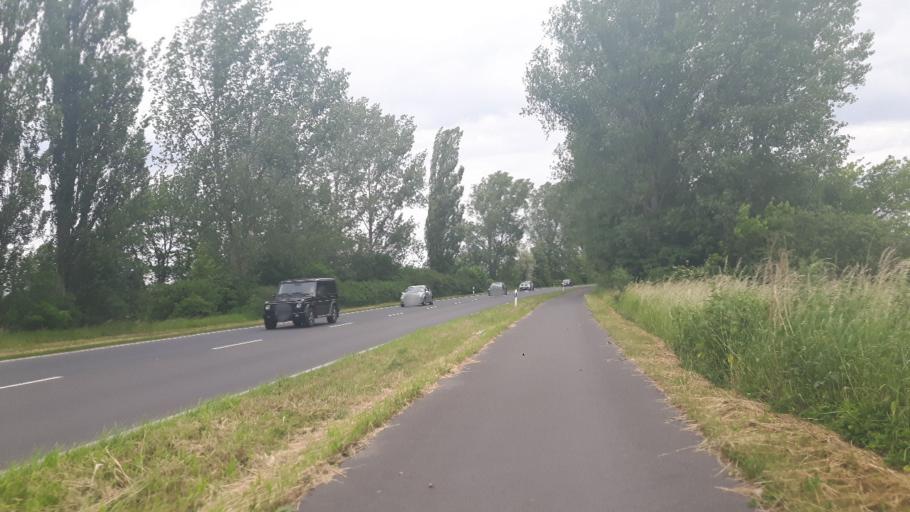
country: DE
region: Berlin
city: Stadtrandsiedlung Malchow
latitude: 52.5892
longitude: 13.4875
